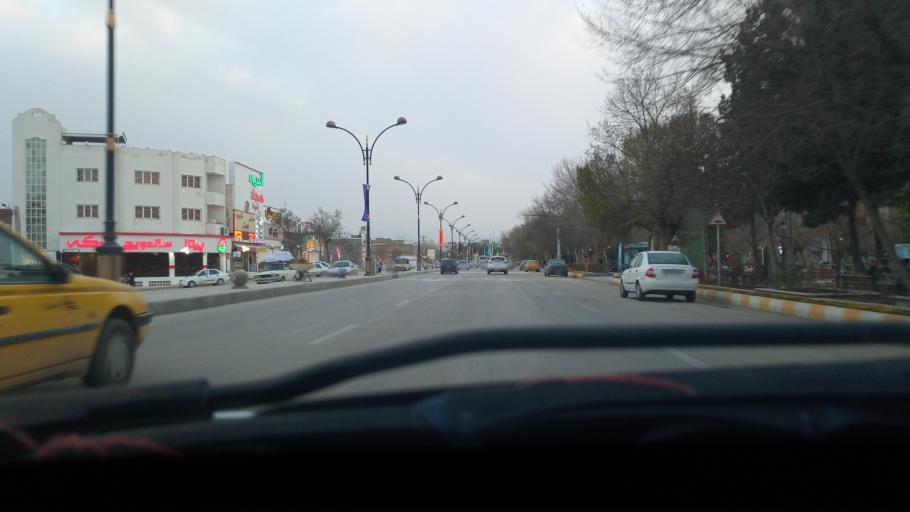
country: IR
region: Khorasan-e Shomali
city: Bojnurd
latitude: 37.4682
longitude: 57.3467
